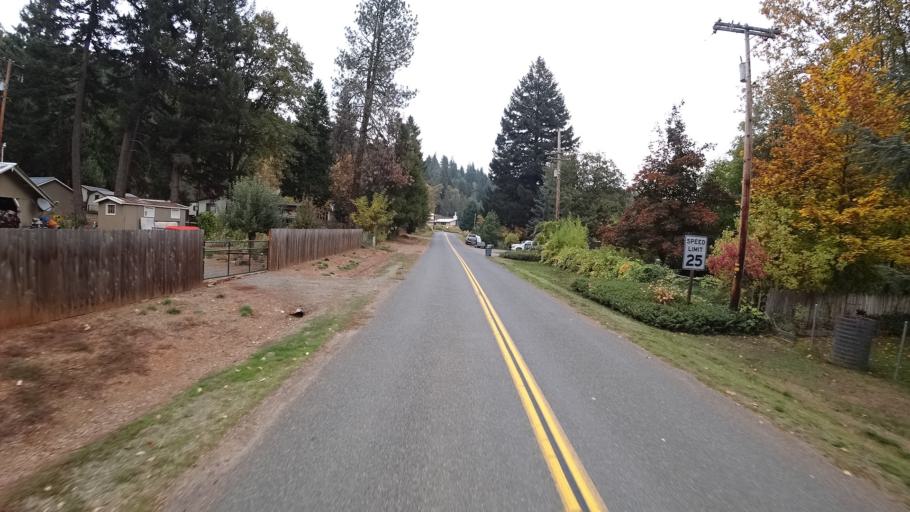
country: US
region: California
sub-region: Siskiyou County
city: Happy Camp
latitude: 41.8077
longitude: -123.3824
